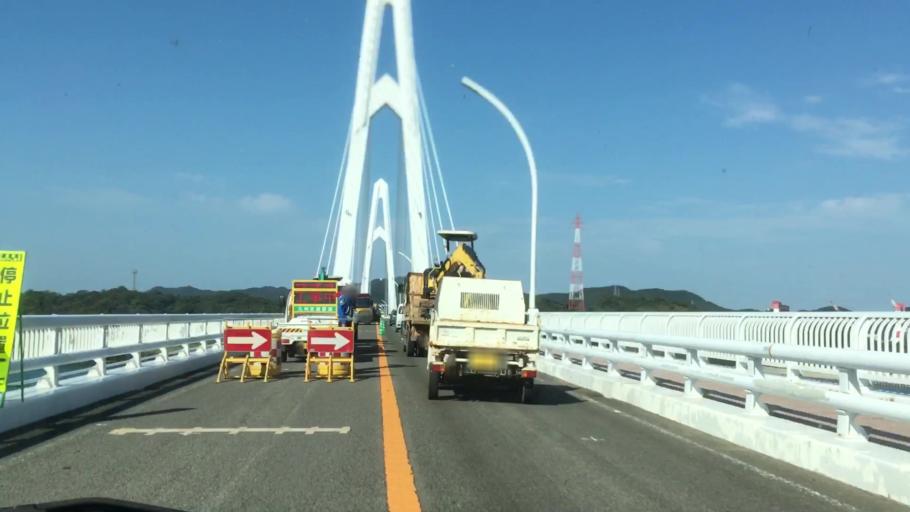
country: JP
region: Nagasaki
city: Sasebo
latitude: 33.0368
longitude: 129.6462
